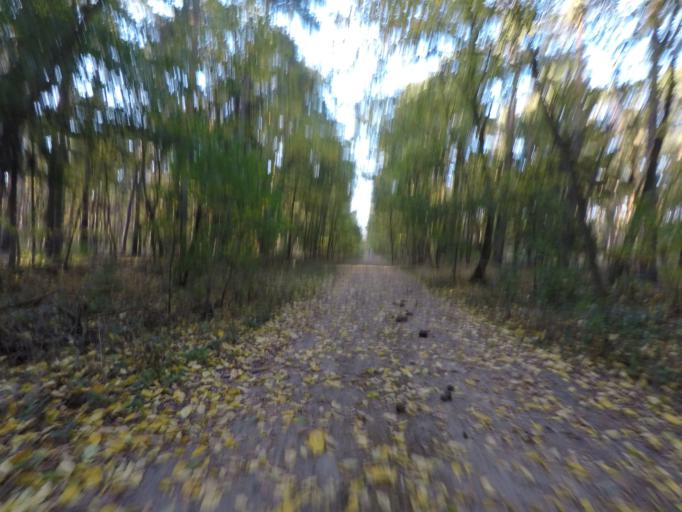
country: DE
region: Brandenburg
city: Biesenthal
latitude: 52.7812
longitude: 13.6398
